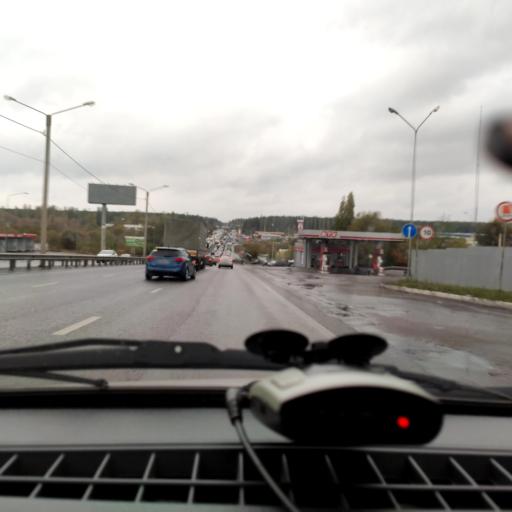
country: RU
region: Voronezj
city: Pridonskoy
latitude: 51.6685
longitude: 39.1250
